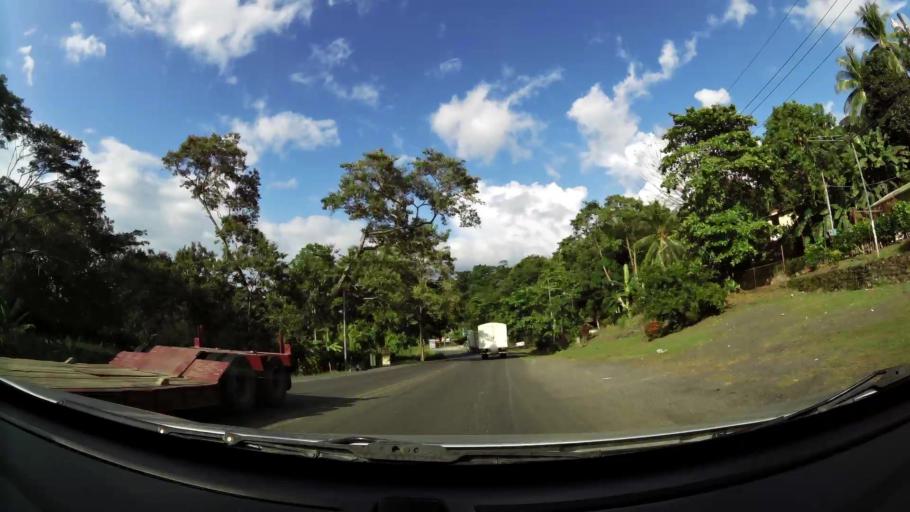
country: CR
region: Puntarenas
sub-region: Canton de Garabito
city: Jaco
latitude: 9.7370
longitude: -84.6311
